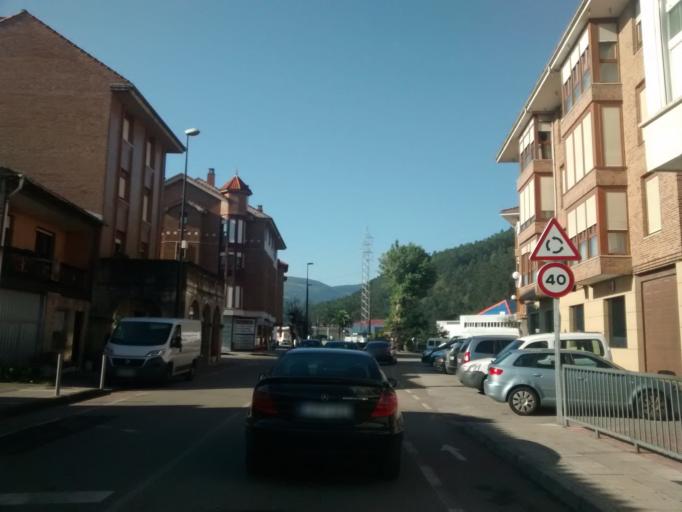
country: ES
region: Cantabria
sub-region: Provincia de Cantabria
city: Cartes
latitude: 43.3343
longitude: -4.0640
